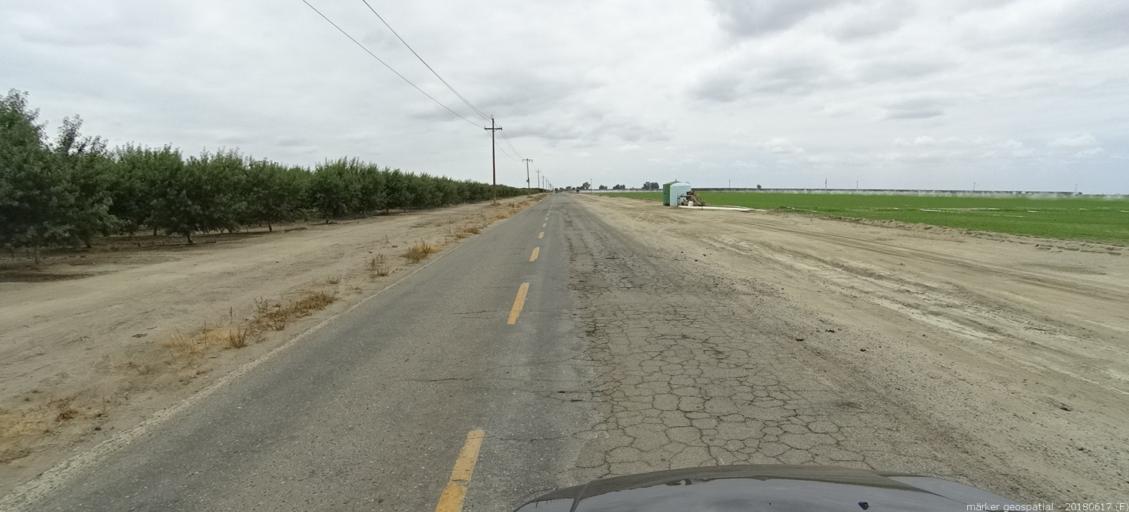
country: US
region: California
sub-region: Madera County
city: Madera
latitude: 36.9207
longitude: -120.1652
